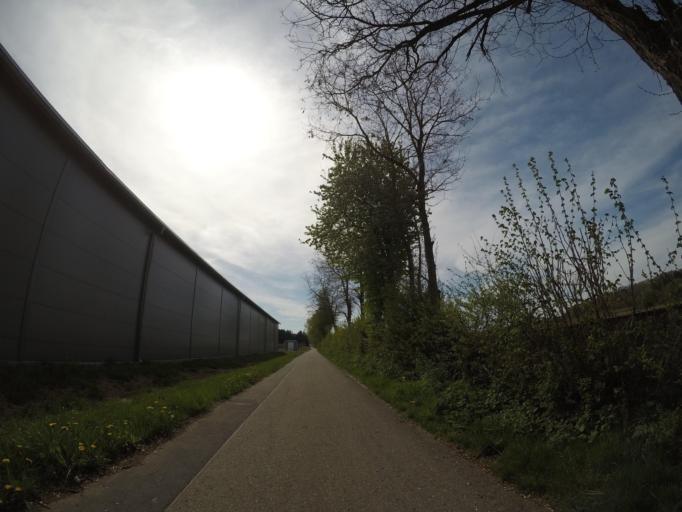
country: DE
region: Baden-Wuerttemberg
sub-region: Tuebingen Region
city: Saulgau
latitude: 48.0008
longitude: 9.5153
